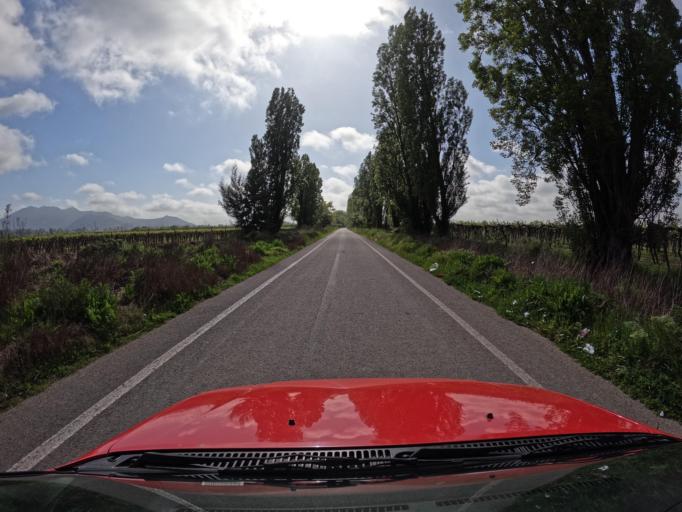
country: CL
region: Maule
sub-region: Provincia de Curico
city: Rauco
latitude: -34.8826
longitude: -71.2460
